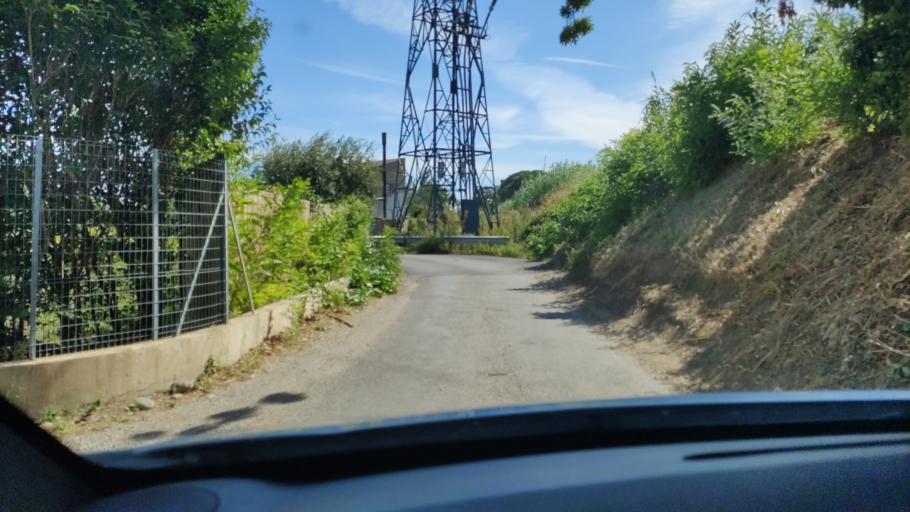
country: FR
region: Provence-Alpes-Cote d'Azur
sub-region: Departement du Vaucluse
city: Morieres-les-Avignon
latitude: 43.9511
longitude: 4.8866
